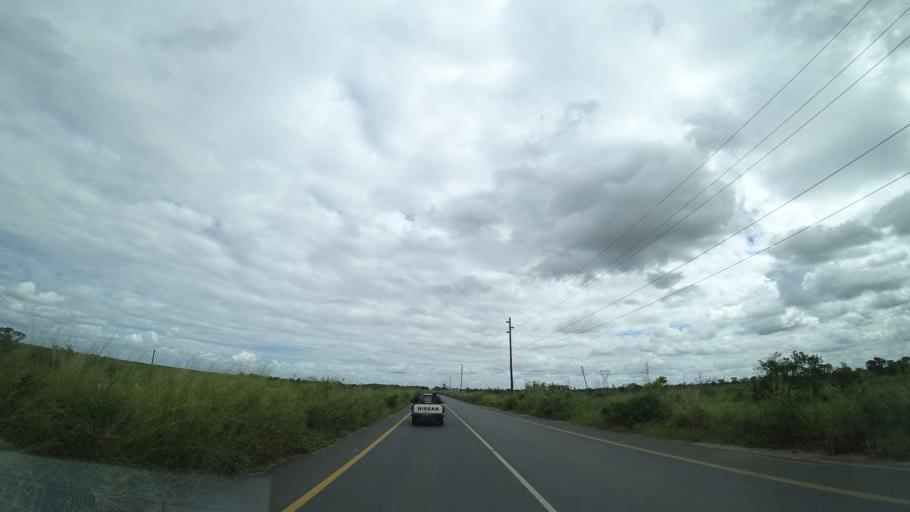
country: MZ
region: Sofala
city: Dondo
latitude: -19.5153
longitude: 34.6183
